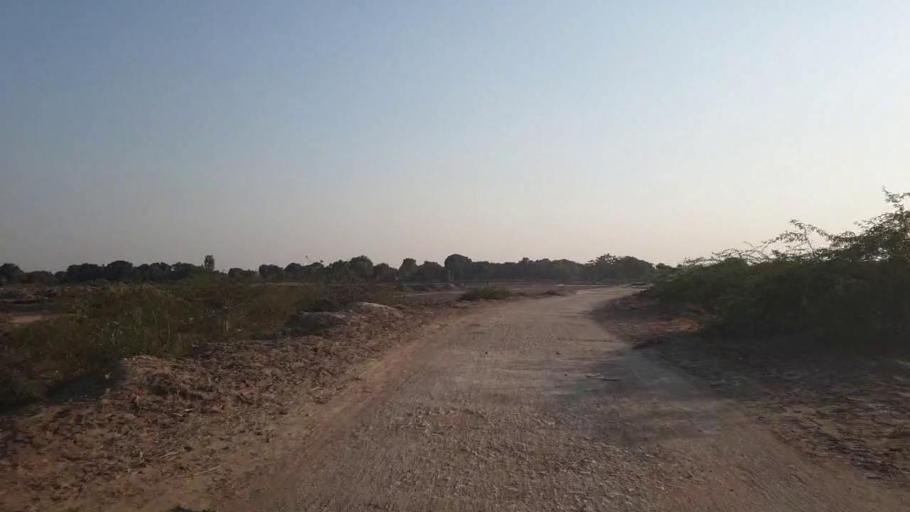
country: PK
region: Sindh
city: Mirpur Khas
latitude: 25.4199
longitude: 68.9069
